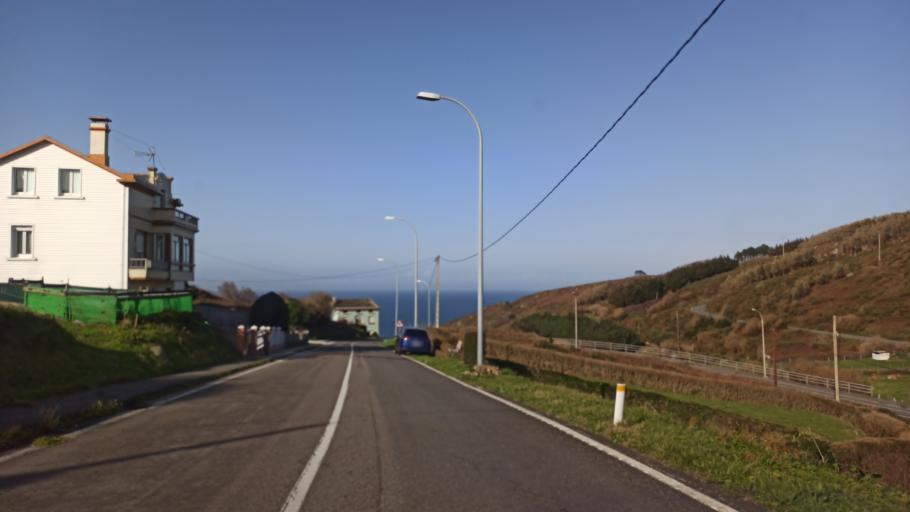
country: ES
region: Galicia
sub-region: Provincia da Coruna
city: Manon
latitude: 43.7723
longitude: -7.6832
